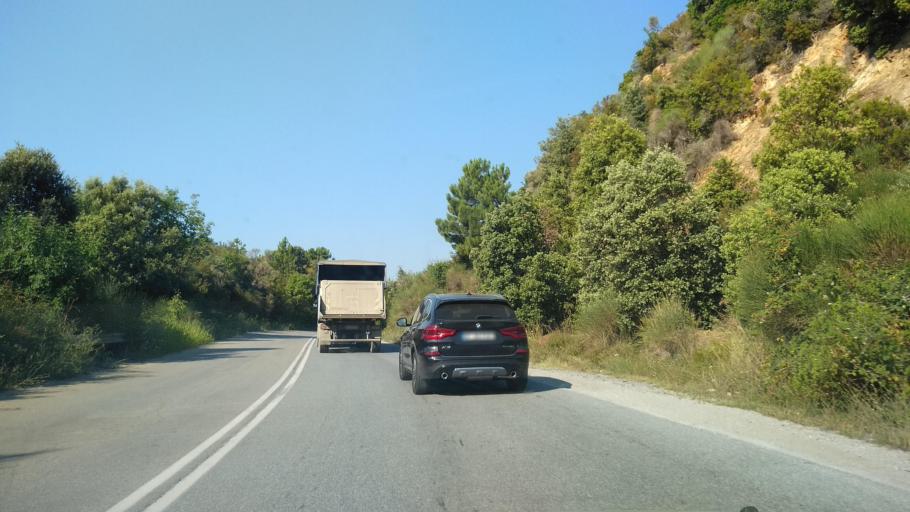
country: GR
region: Central Macedonia
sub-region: Nomos Chalkidikis
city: Stratonion
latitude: 40.5199
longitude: 23.8168
